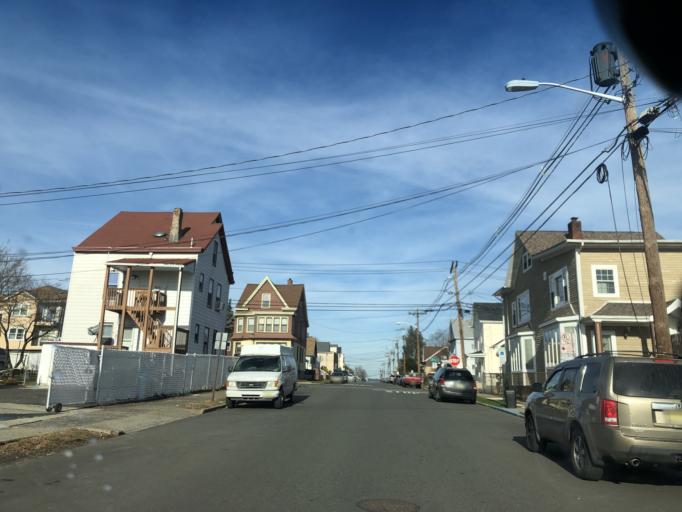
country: US
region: New Jersey
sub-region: Bergen County
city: Fair Lawn
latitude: 40.9310
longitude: -74.1460
